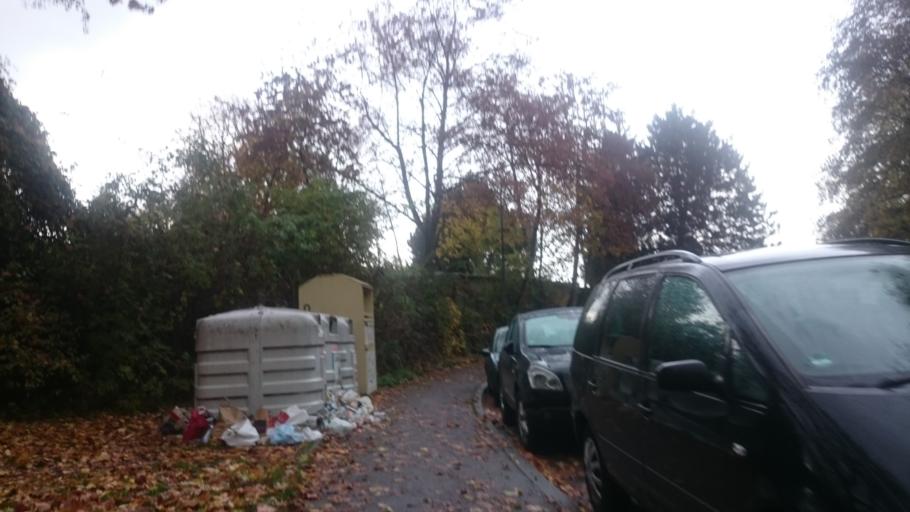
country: DE
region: Bavaria
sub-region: Swabia
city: Augsburg
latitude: 48.3565
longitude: 10.9221
